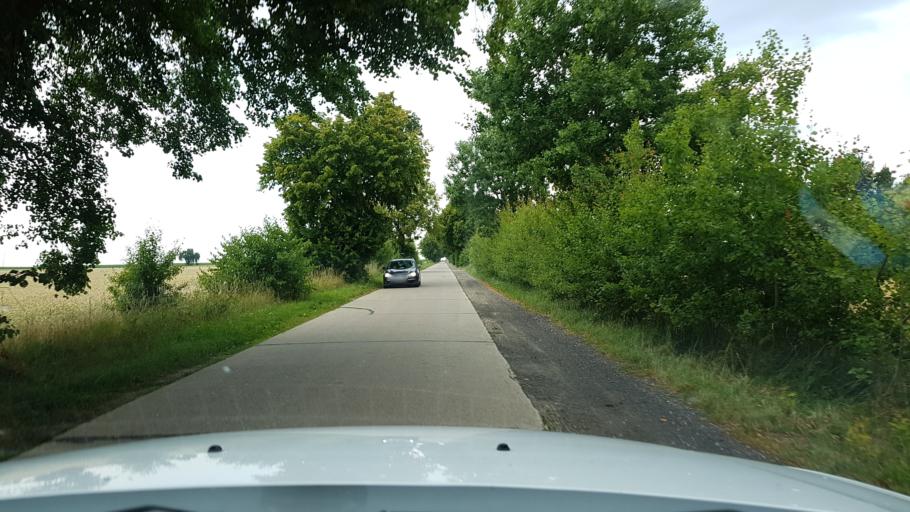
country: PL
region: West Pomeranian Voivodeship
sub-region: Powiat walecki
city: Walcz
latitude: 53.3545
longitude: 16.3476
